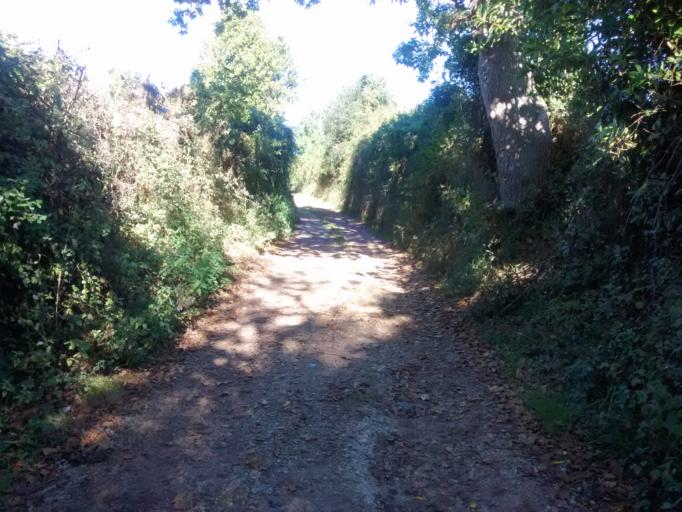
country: ES
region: Asturias
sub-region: Province of Asturias
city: Colunga
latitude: 43.4659
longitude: -5.2368
